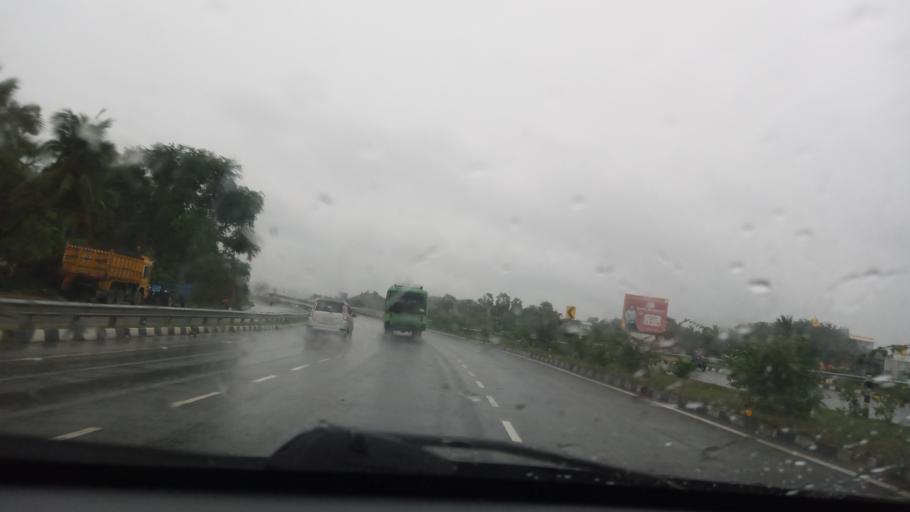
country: IN
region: Tamil Nadu
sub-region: Vellore
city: Arcot
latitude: 12.9386
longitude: 79.2482
